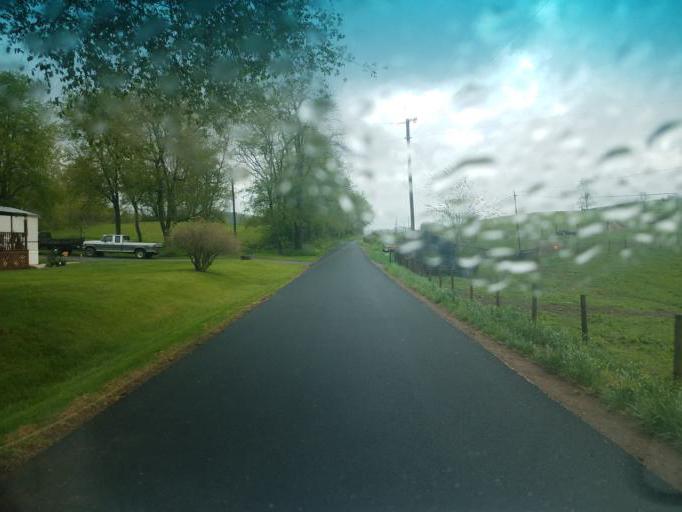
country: US
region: Virginia
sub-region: Smyth County
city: Marion
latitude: 36.9318
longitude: -81.5348
